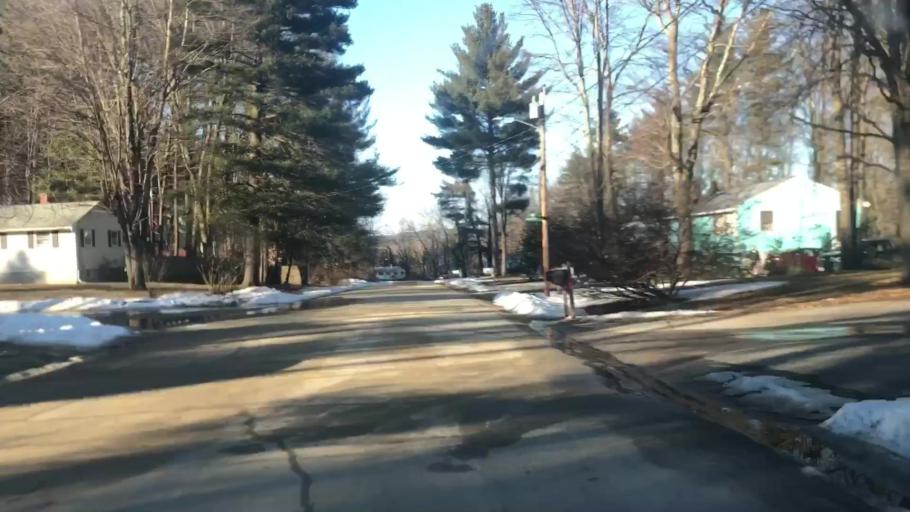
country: US
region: New Hampshire
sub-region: Hillsborough County
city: Milford
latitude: 42.8338
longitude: -71.6691
